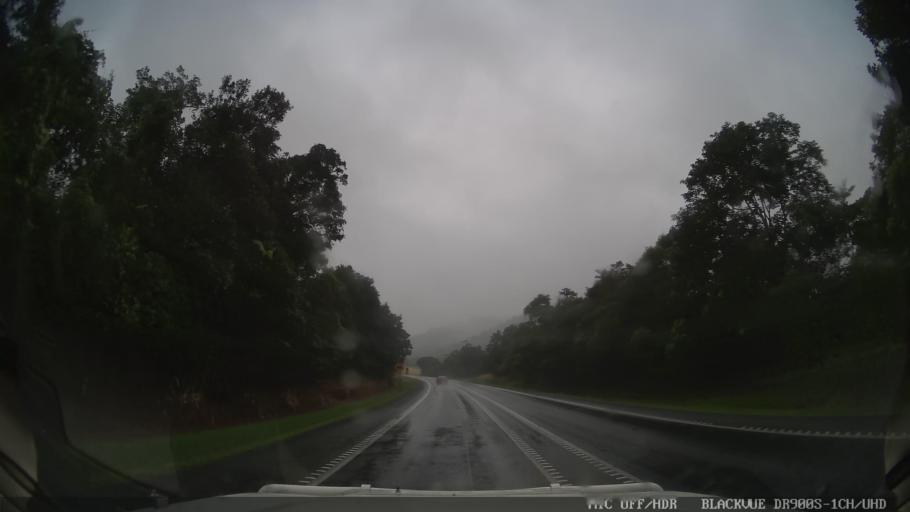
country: AU
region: Queensland
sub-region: Cassowary Coast
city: Innisfail
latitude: -17.8626
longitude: 145.9852
